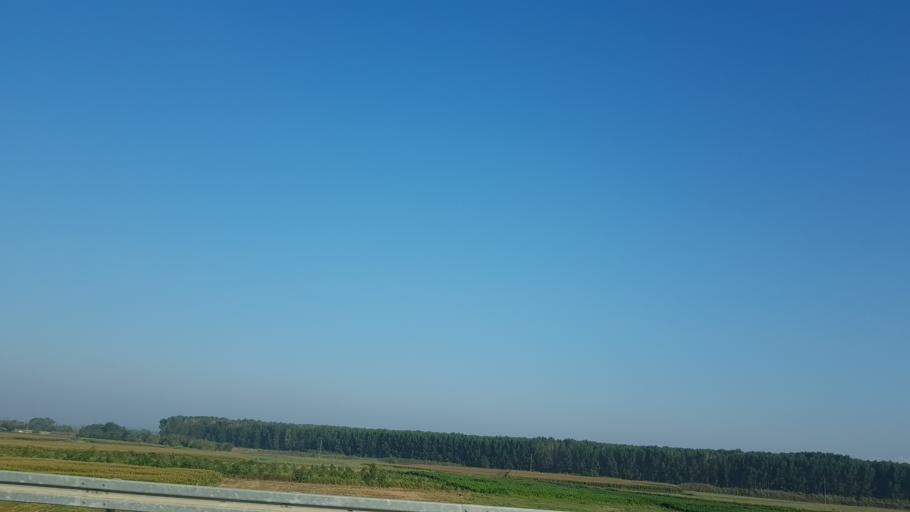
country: TR
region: Bursa
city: Karacabey
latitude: 40.1420
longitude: 28.3031
